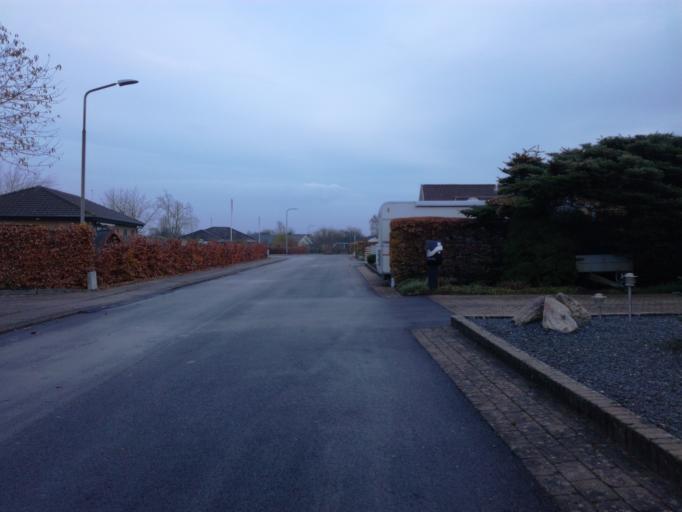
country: DK
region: South Denmark
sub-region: Vejle Kommune
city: Borkop
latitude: 55.6382
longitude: 9.6477
